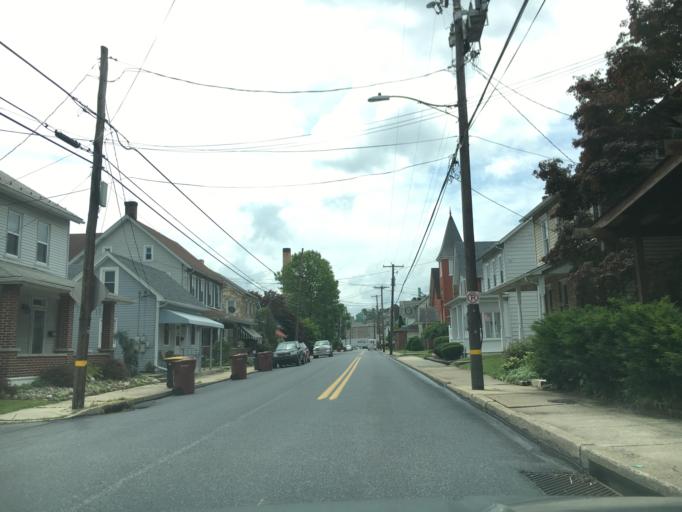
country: US
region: Pennsylvania
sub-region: Lehigh County
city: Cementon
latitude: 40.6910
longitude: -75.5091
